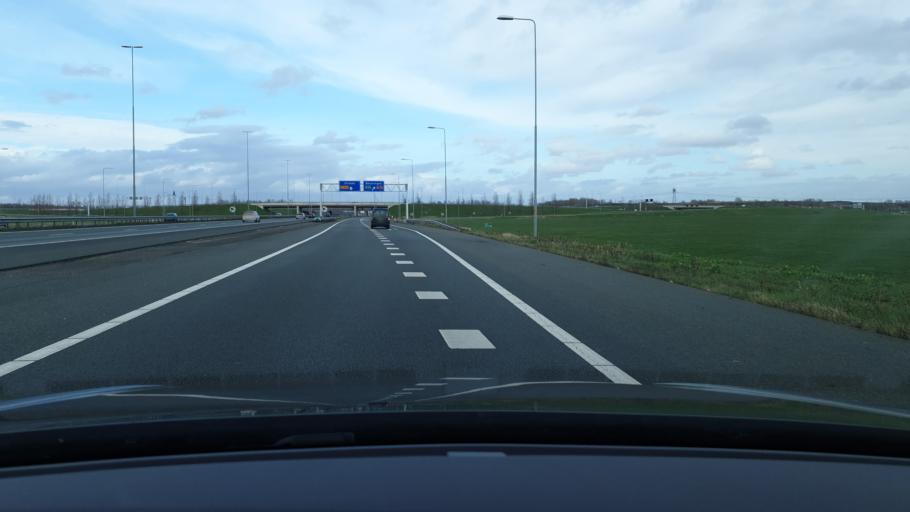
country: NL
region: Gelderland
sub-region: Gemeente Wijchen
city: Bergharen
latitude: 51.8535
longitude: 5.7062
